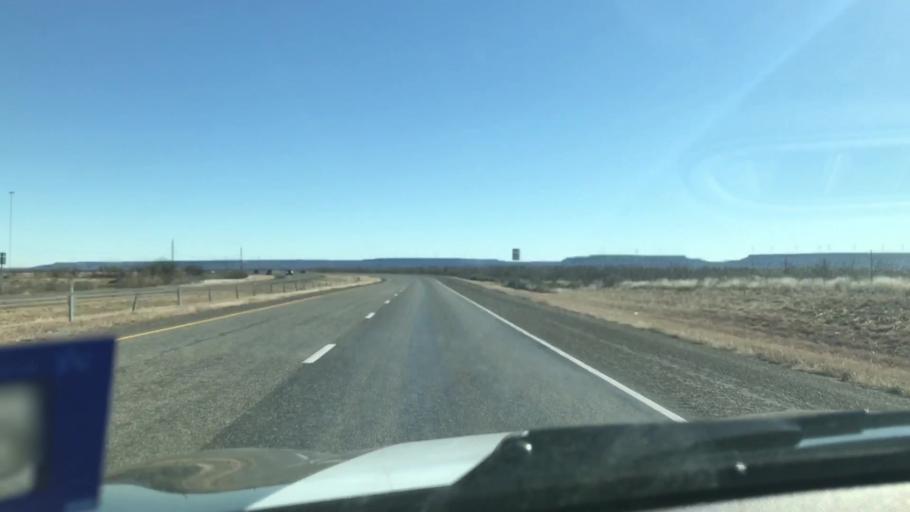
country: US
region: Texas
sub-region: Garza County
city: Post
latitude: 33.0767
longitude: -101.2382
